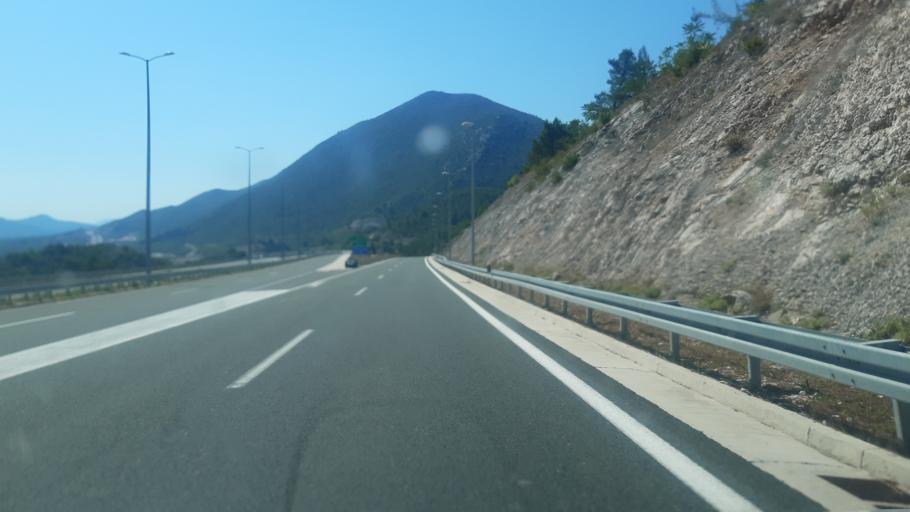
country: BA
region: Federation of Bosnia and Herzegovina
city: Ljubuski
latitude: 43.1522
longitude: 17.4814
